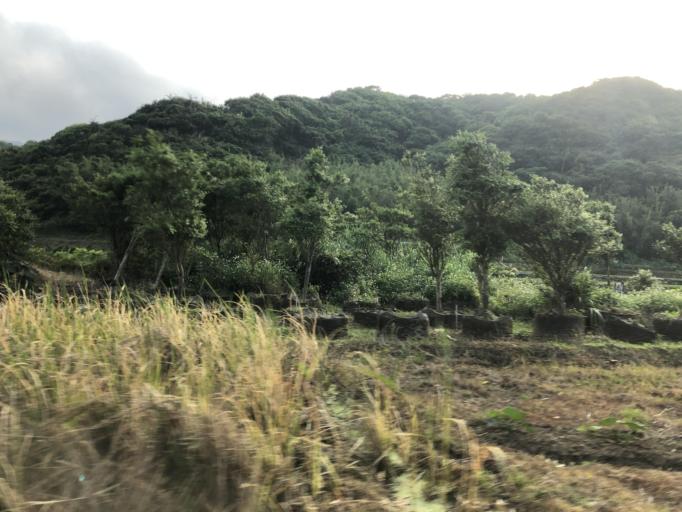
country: TW
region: Taiwan
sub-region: Keelung
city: Keelung
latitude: 25.2077
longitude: 121.6472
